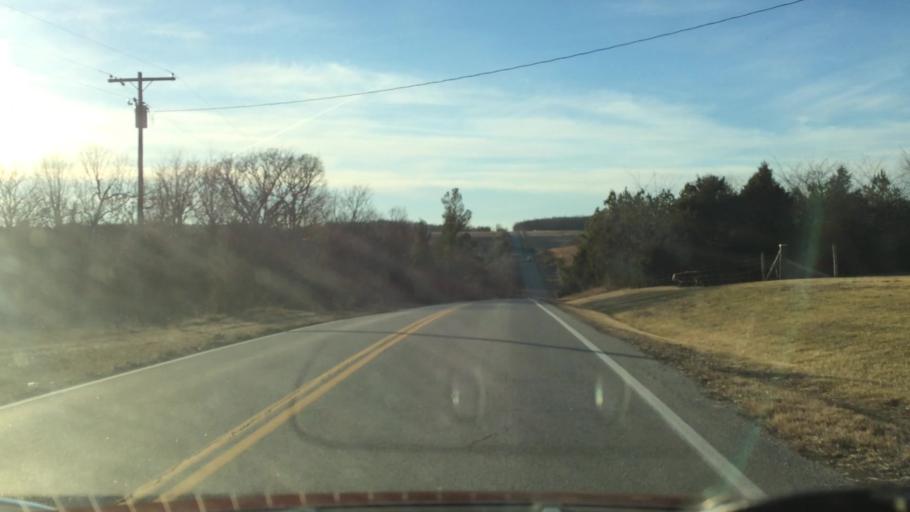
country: US
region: Missouri
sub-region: Webster County
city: Marshfield
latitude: 37.3406
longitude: -92.9628
